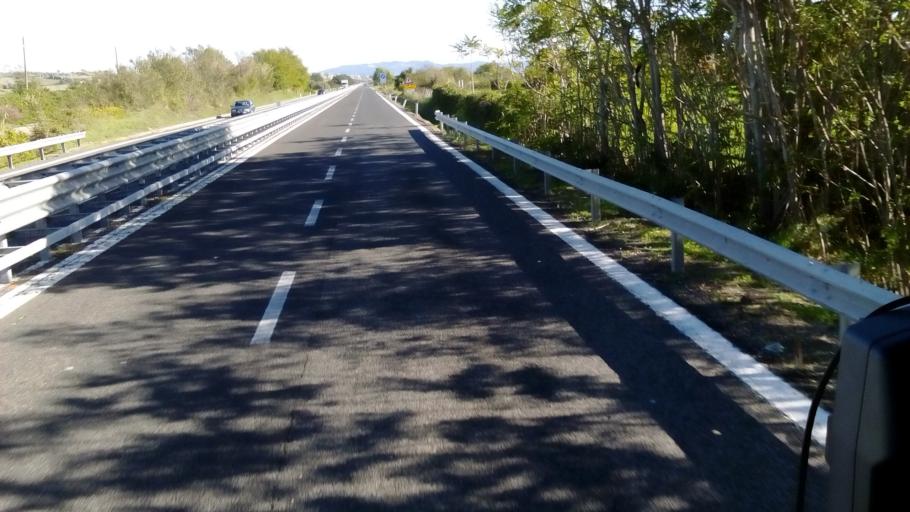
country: IT
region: Latium
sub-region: Provincia di Viterbo
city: Tarquinia
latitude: 42.2813
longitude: 11.6947
